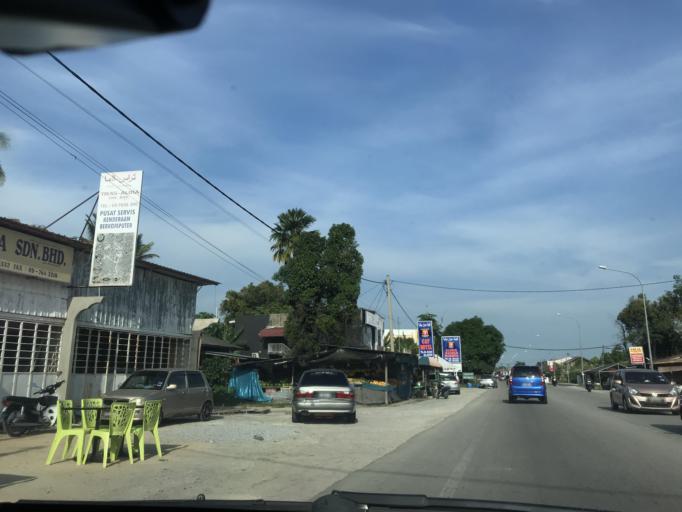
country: MY
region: Kelantan
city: Kota Bharu
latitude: 6.1217
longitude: 102.2839
